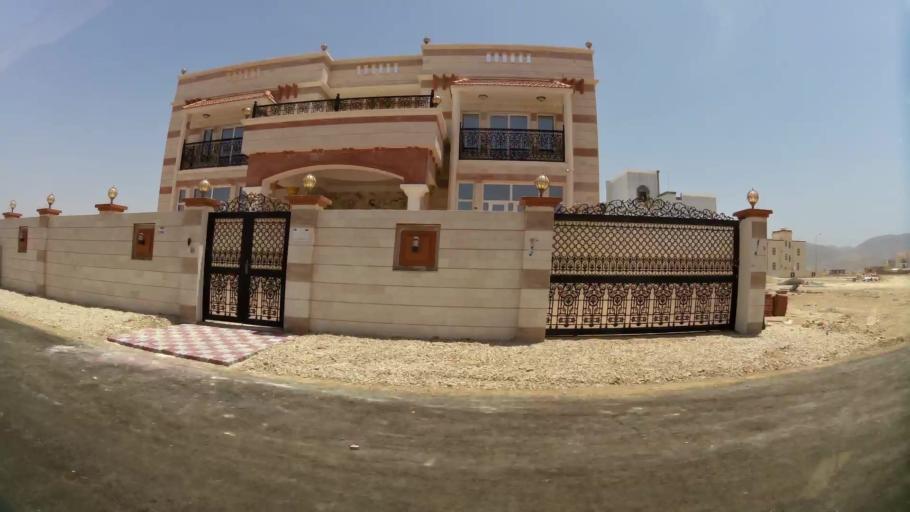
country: OM
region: Zufar
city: Salalah
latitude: 17.0993
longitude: 54.2082
